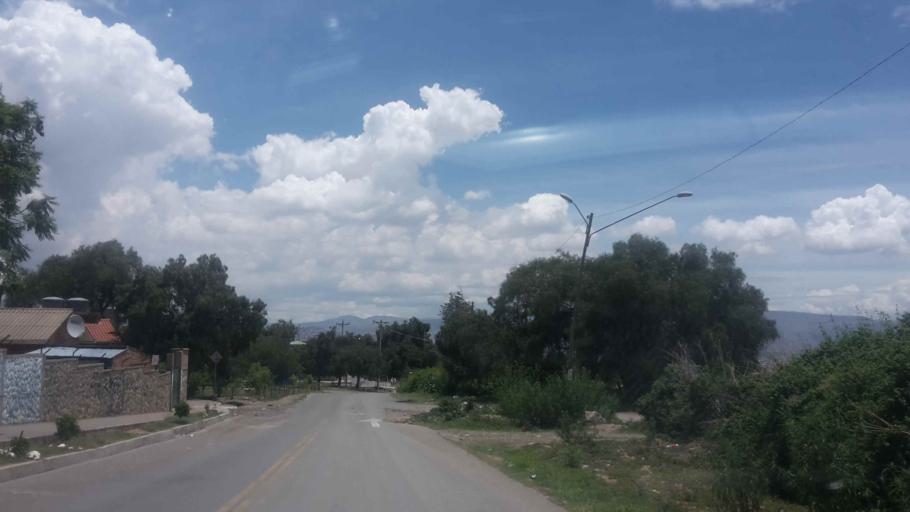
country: BO
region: Cochabamba
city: Cochabamba
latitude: -17.3437
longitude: -66.1785
